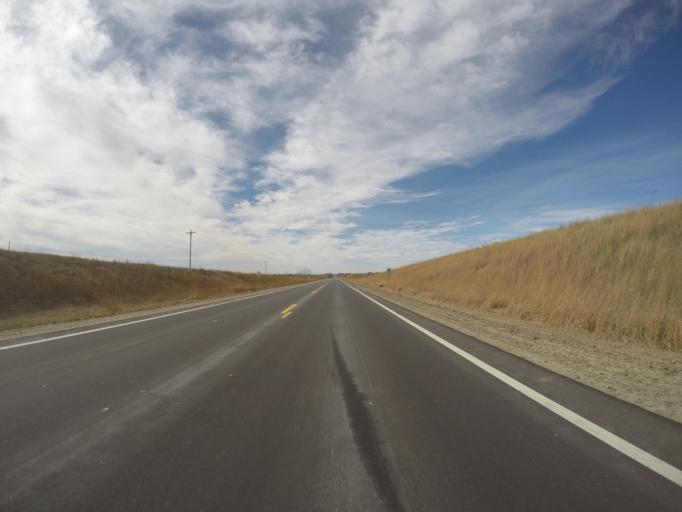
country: US
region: Nebraska
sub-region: Franklin County
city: Franklin
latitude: 40.0968
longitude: -98.7881
